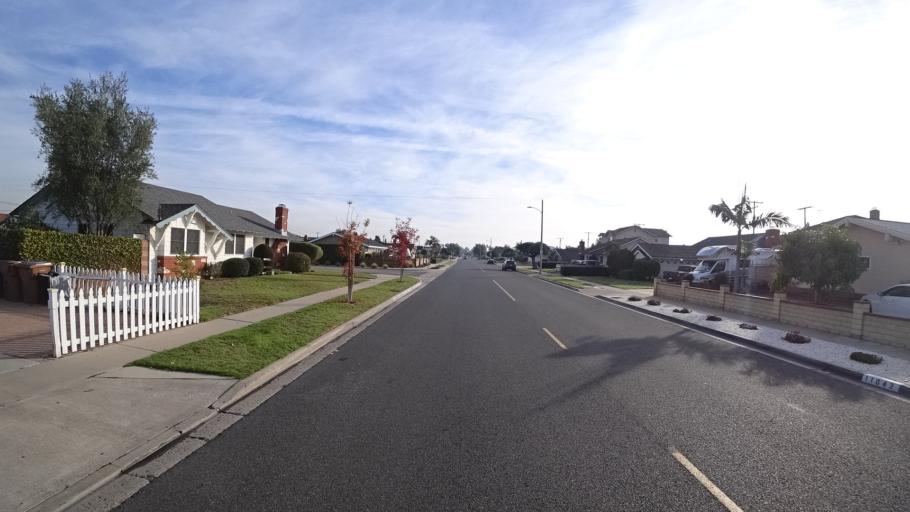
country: US
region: California
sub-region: Orange County
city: Garden Grove
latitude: 33.7937
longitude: -117.9300
